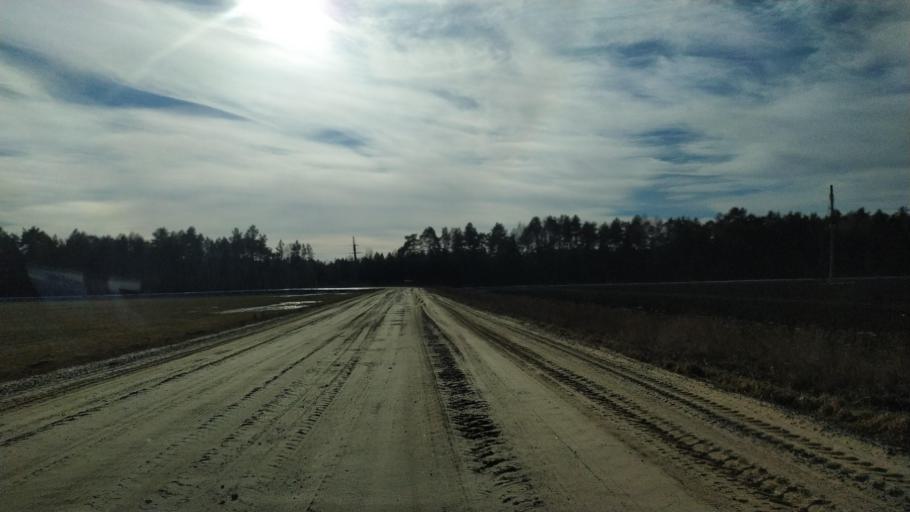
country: BY
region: Brest
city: Pruzhany
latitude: 52.5598
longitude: 24.2920
